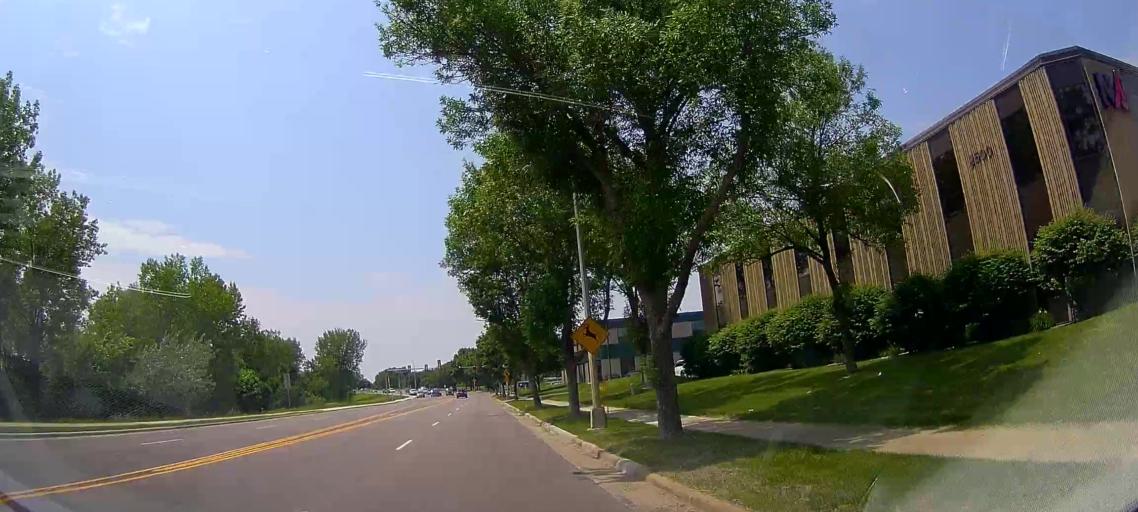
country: US
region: South Dakota
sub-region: Minnehaha County
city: Sioux Falls
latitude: 43.5085
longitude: -96.7564
